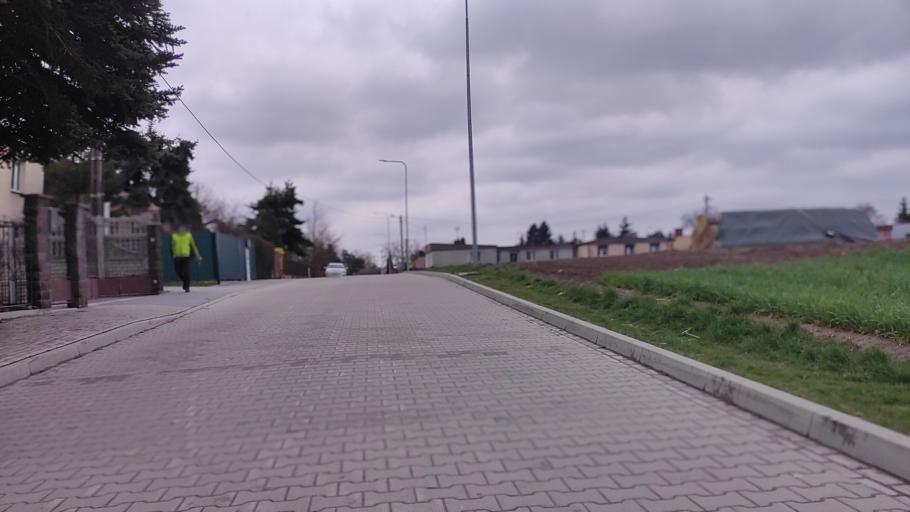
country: PL
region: Greater Poland Voivodeship
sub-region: Powiat poznanski
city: Kostrzyn
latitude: 52.4000
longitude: 17.1626
